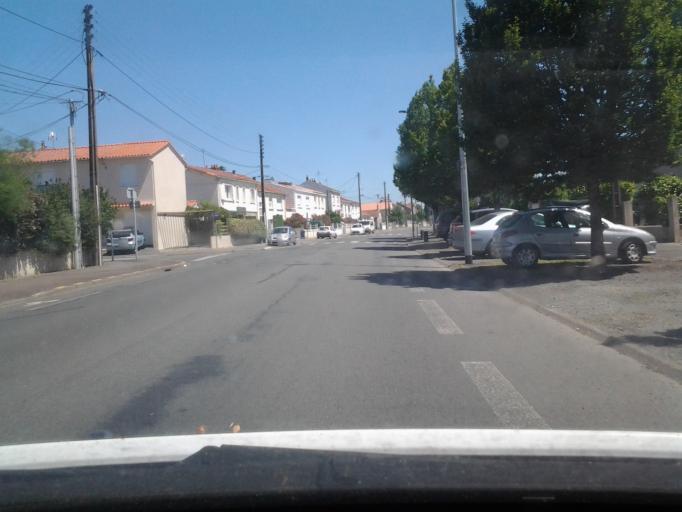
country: FR
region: Pays de la Loire
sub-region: Departement de la Vendee
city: La Roche-sur-Yon
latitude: 46.6591
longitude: -1.4353
